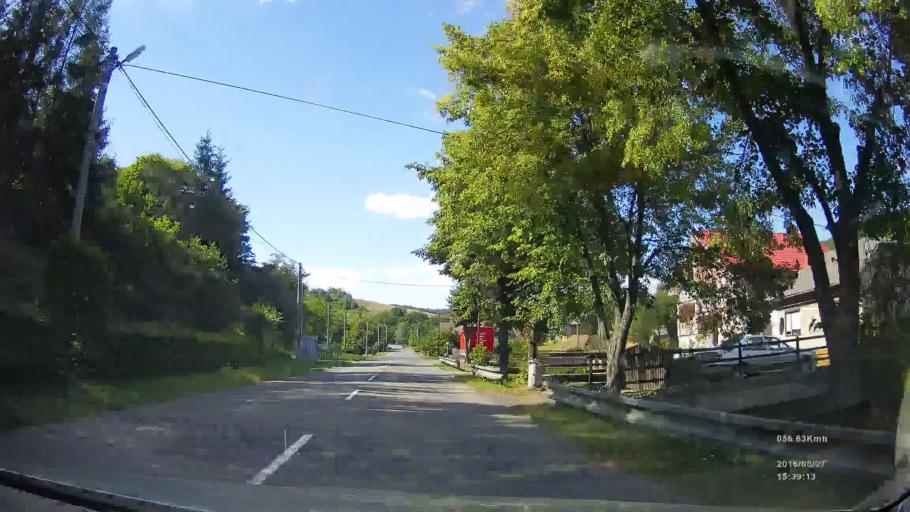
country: SK
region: Presovsky
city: Giraltovce
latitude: 49.1165
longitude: 21.6052
